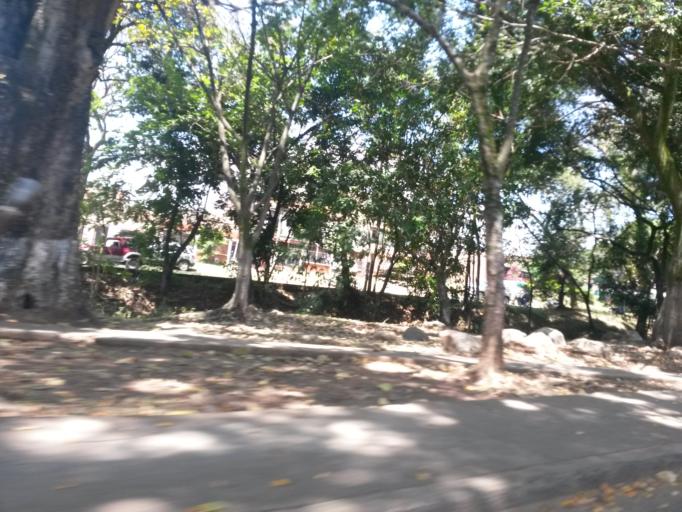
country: CO
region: Cauca
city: Santander de Quilichao
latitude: 3.0081
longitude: -76.4806
